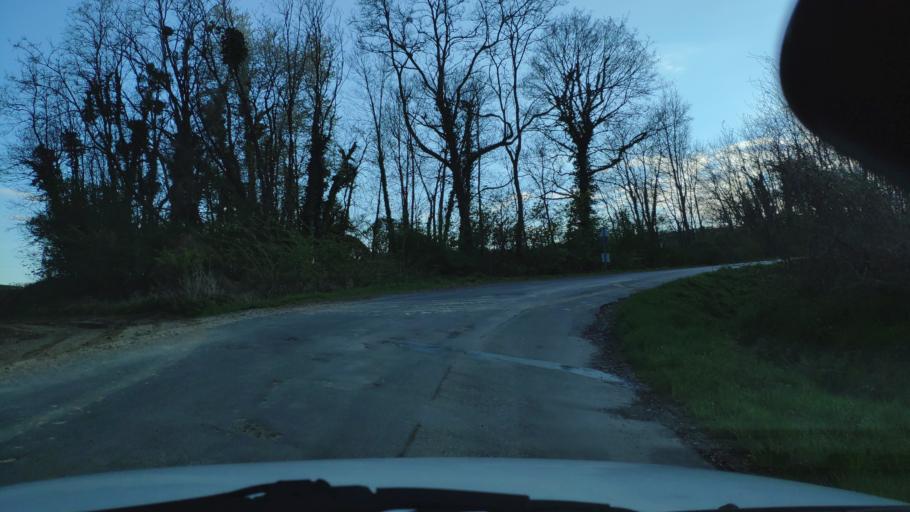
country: HU
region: Zala
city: Nagykanizsa
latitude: 46.4206
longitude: 17.1056
